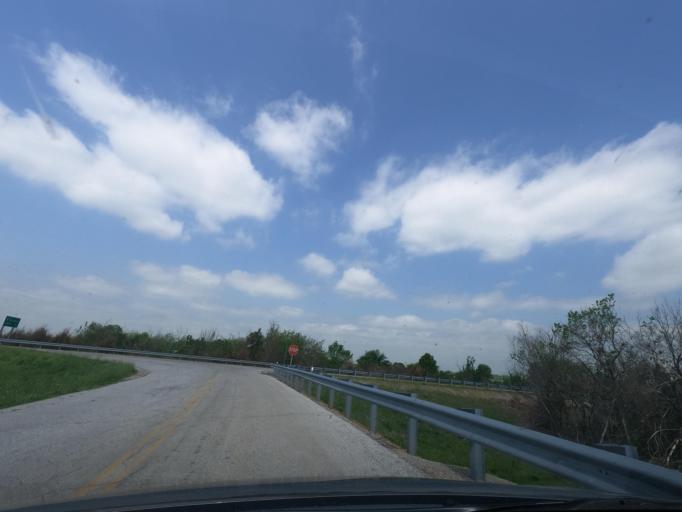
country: US
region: Missouri
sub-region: Lawrence County
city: Mount Vernon
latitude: 37.0763
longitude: -93.9497
